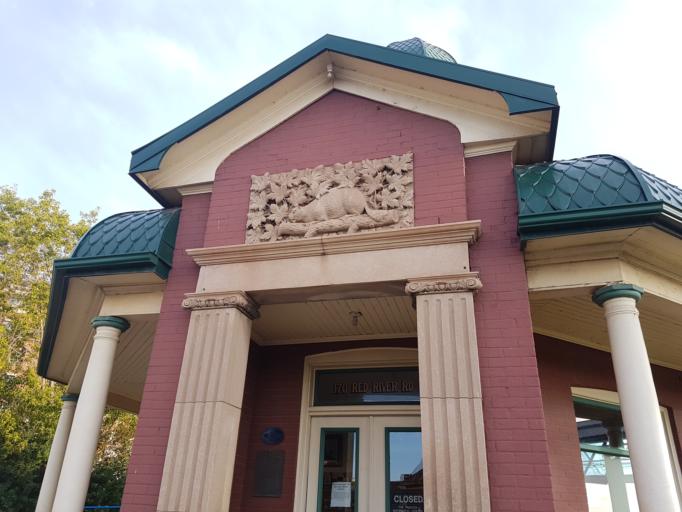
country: CA
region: Ontario
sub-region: Thunder Bay District
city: Thunder Bay
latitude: 48.4345
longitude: -89.2181
